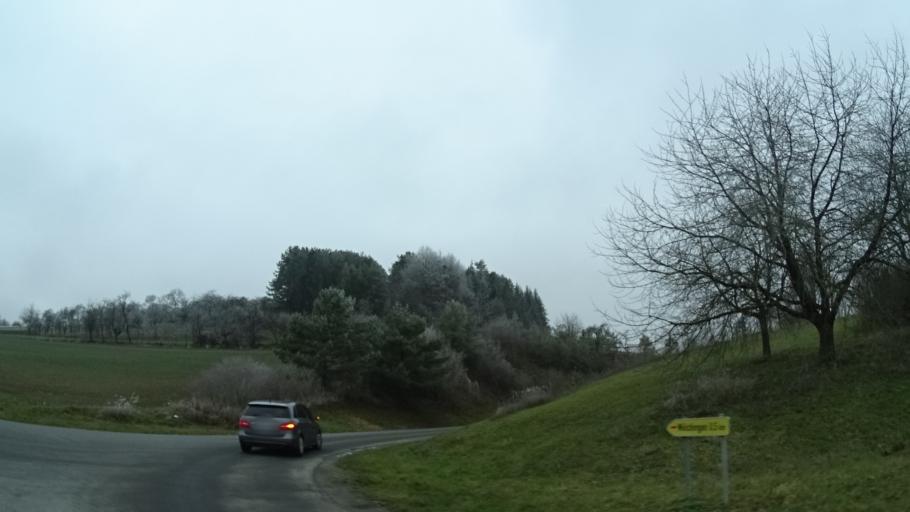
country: DE
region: Baden-Wuerttemberg
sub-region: Regierungsbezirk Stuttgart
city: Boxberg
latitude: 49.4801
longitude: 9.6329
